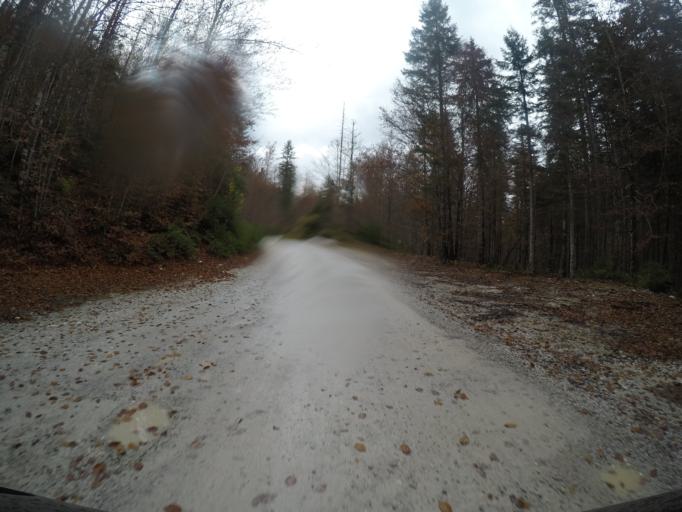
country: SI
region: Kranjska Gora
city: Mojstrana
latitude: 46.4184
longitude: 13.8584
